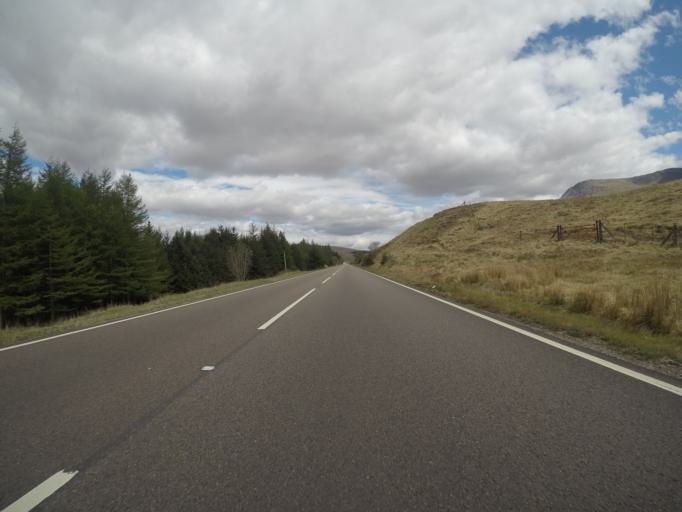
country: GB
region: Scotland
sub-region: Highland
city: Spean Bridge
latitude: 56.5425
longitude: -4.7631
